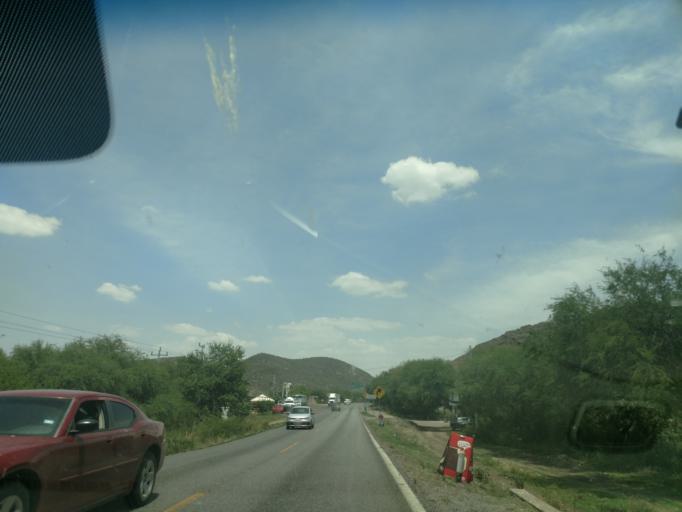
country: MX
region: San Luis Potosi
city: Ciudad Fernandez
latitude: 22.0062
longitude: -100.1490
